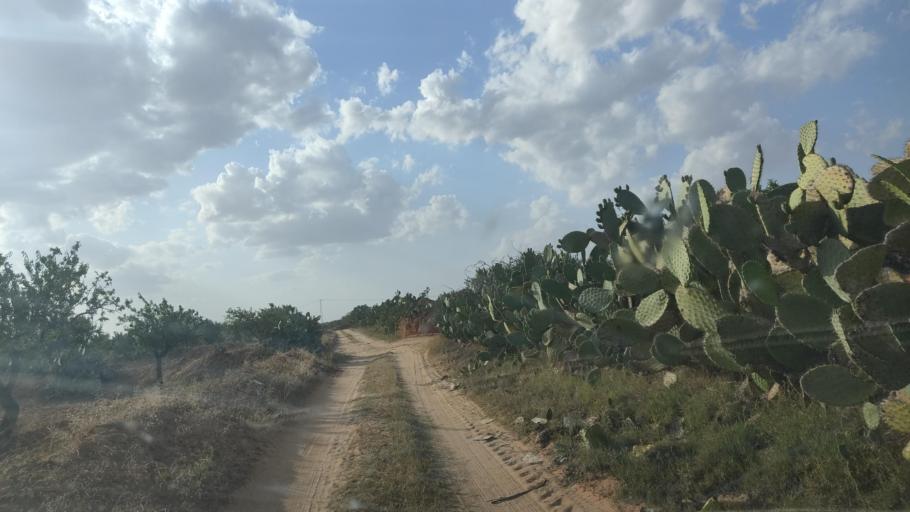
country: TN
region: Safaqis
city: Sfax
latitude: 34.8536
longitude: 10.5919
